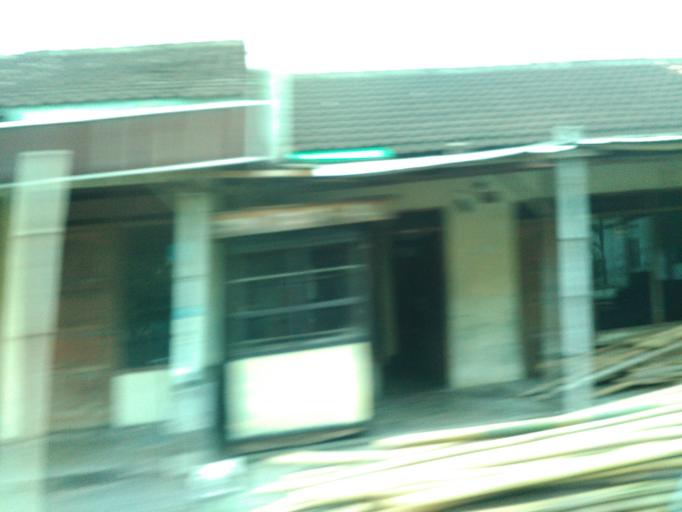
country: ID
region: Central Java
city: Delanggu
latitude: -7.6220
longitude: 110.7027
